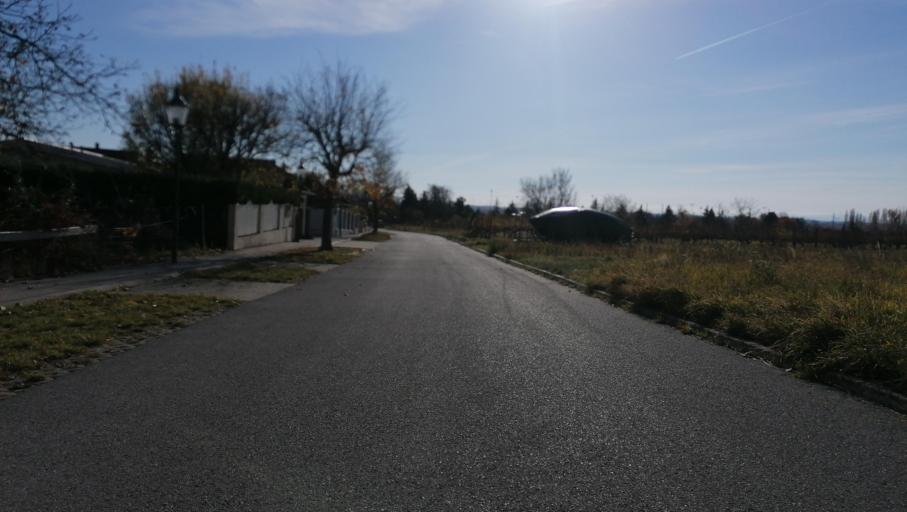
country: AT
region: Lower Austria
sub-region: Politischer Bezirk Modling
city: Gumpoldskirchen
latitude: 48.0401
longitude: 16.2794
